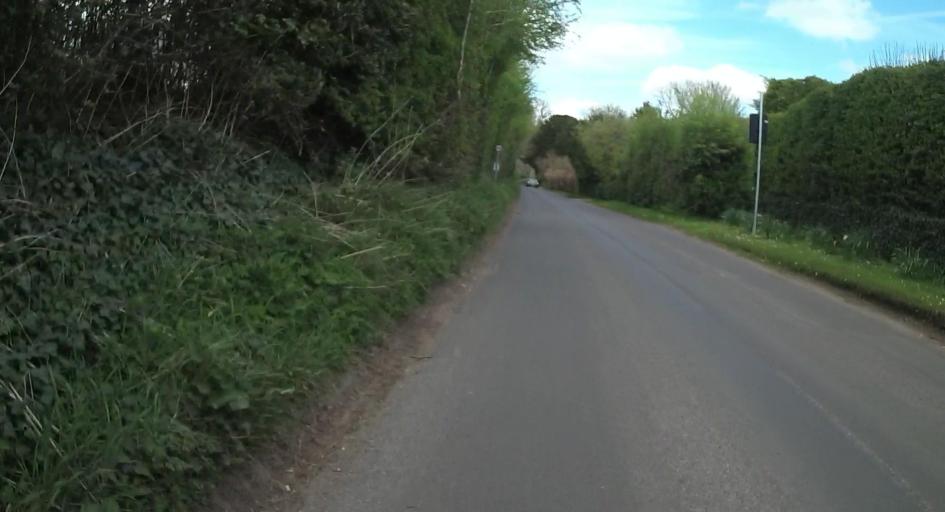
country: GB
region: England
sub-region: Hampshire
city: Abbotts Ann
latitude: 51.0923
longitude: -1.5113
